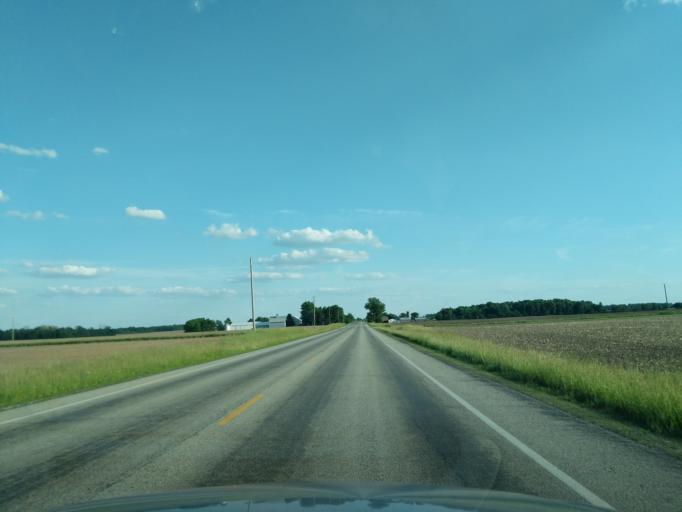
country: US
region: Indiana
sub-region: Huntington County
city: Huntington
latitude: 40.9774
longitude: -85.4715
